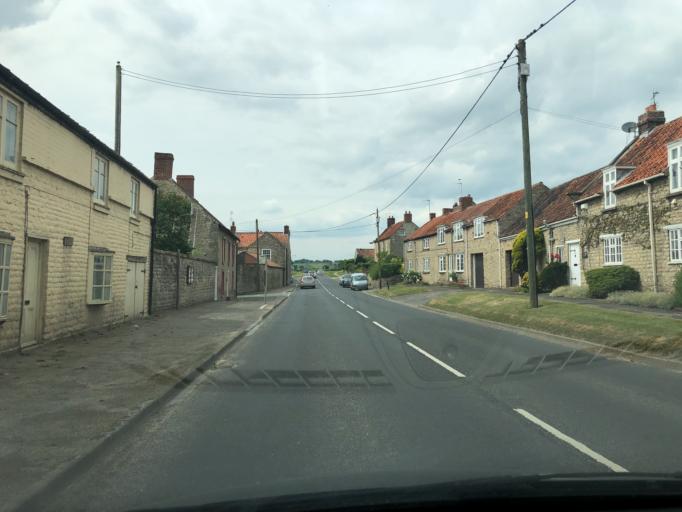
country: GB
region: England
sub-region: North Yorkshire
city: Pickering
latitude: 54.2612
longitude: -0.8114
